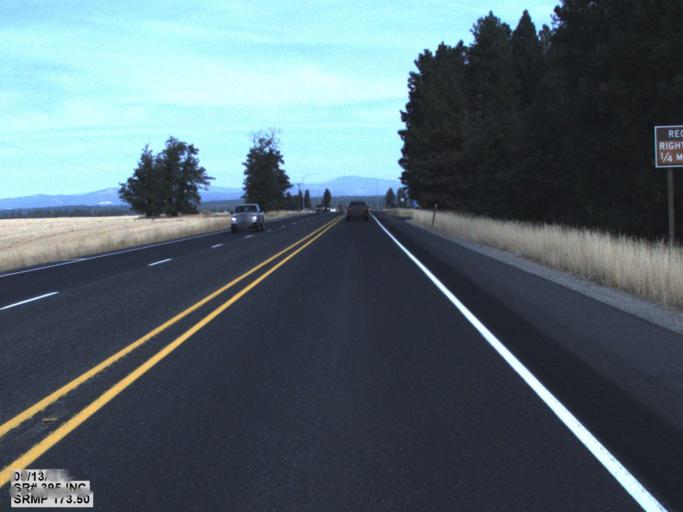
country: US
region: Washington
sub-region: Spokane County
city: Fairwood
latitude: 47.8659
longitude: -117.4220
